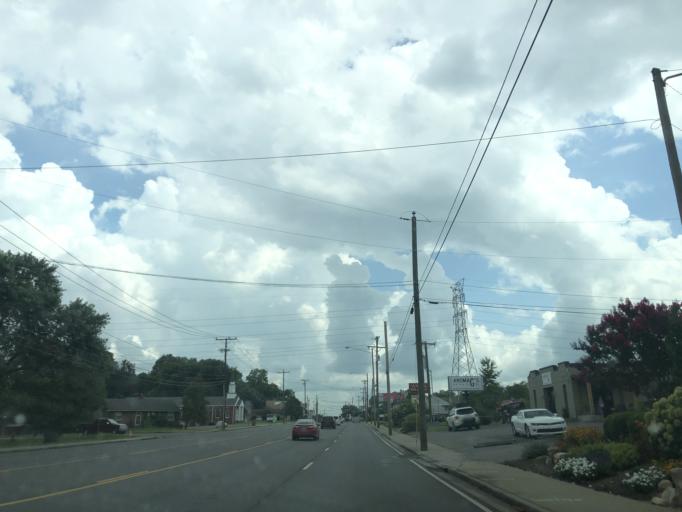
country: US
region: Tennessee
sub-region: Davidson County
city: Lakewood
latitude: 36.1598
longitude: -86.6645
